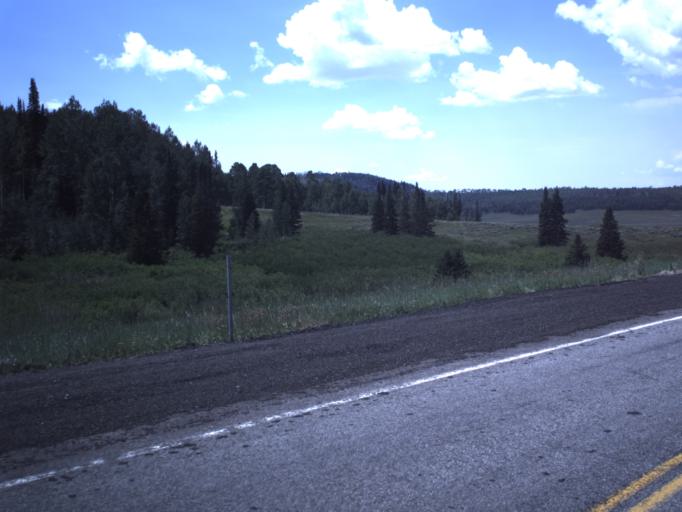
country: US
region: Utah
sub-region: Sanpete County
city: Fairview
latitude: 39.6558
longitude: -111.2978
